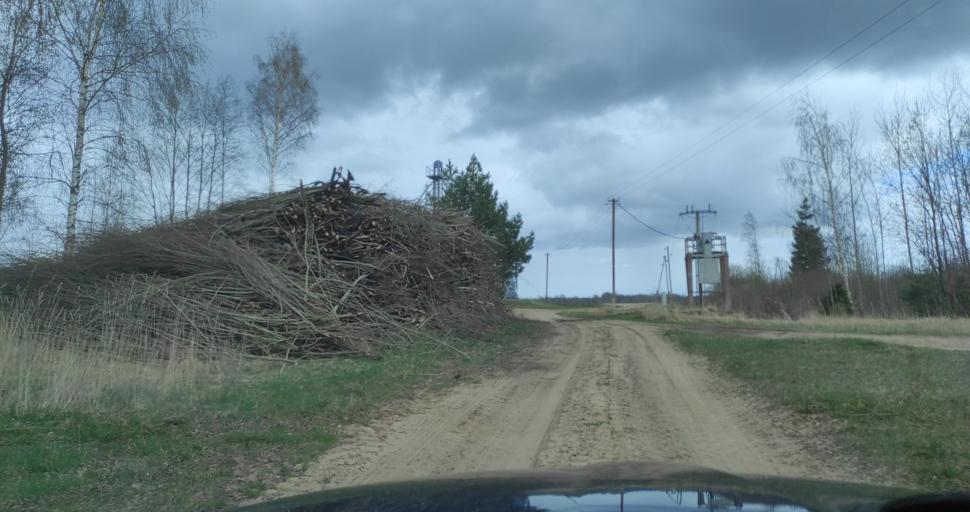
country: LV
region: Aizpute
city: Aizpute
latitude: 56.8249
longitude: 21.7716
